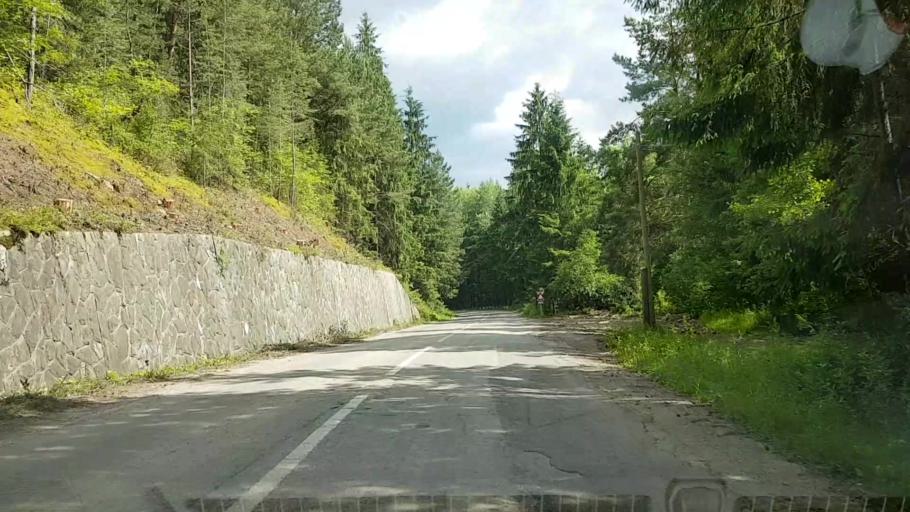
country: RO
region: Neamt
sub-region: Comuna Hangu
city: Hangu
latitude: 47.0522
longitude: 26.0056
